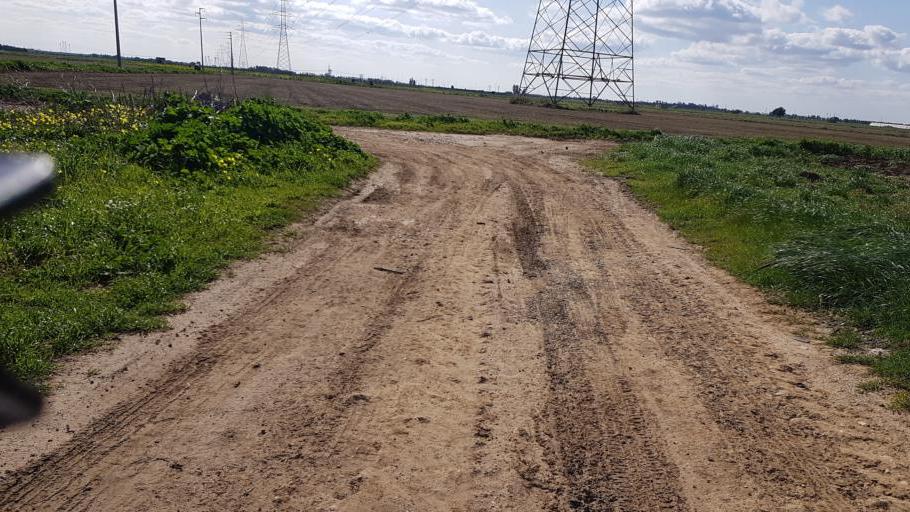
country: IT
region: Apulia
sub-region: Provincia di Brindisi
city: Tuturano
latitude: 40.5752
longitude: 17.9082
